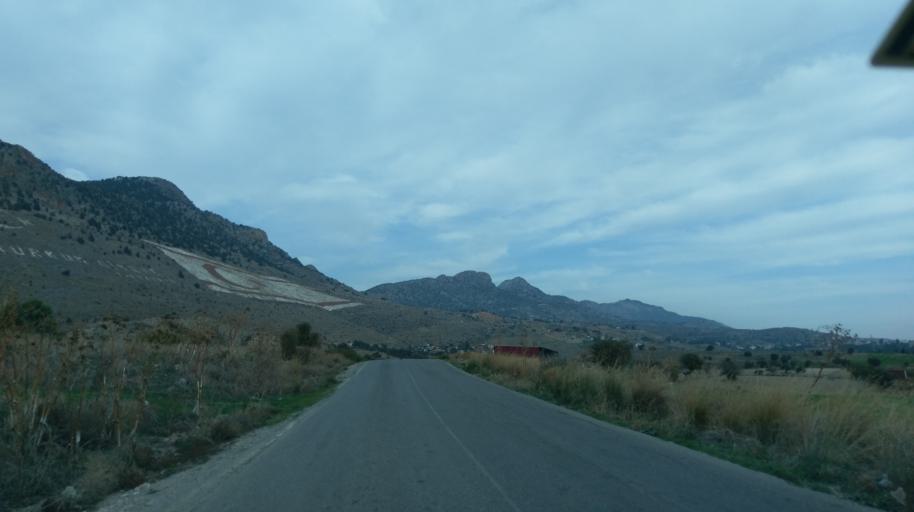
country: CY
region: Keryneia
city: Kyrenia
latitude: 35.2733
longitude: 33.3636
